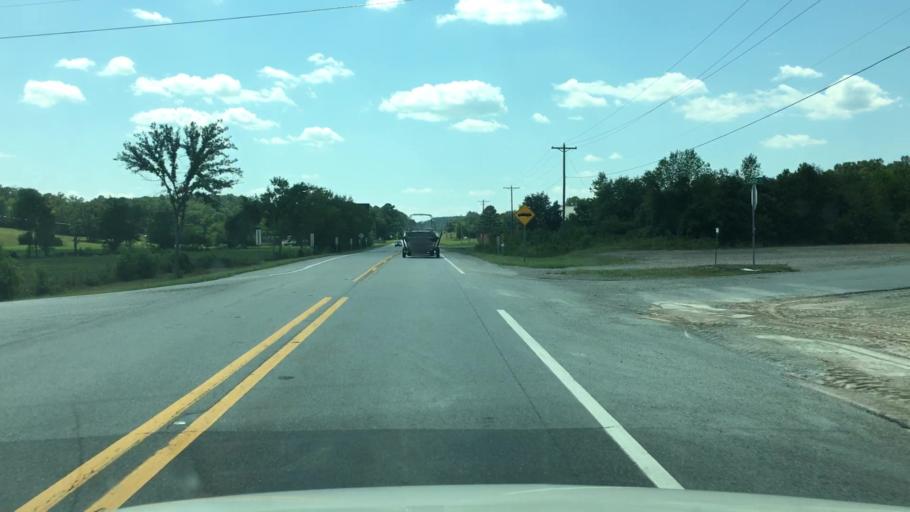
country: US
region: Arkansas
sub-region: Garland County
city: Piney
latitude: 34.5107
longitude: -93.2185
